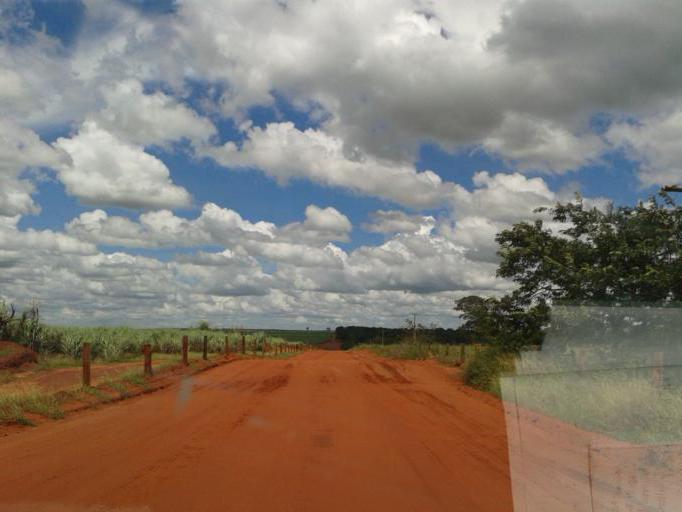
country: BR
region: Minas Gerais
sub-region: Santa Vitoria
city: Santa Vitoria
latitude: -18.8288
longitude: -50.0683
